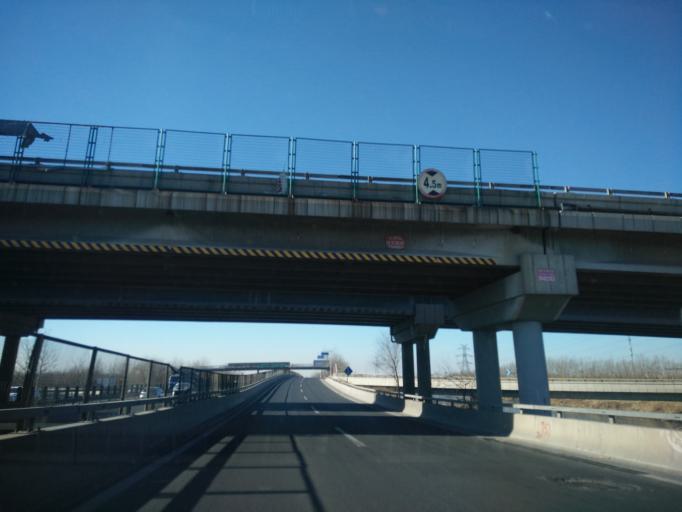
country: CN
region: Beijing
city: Qingyundian
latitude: 39.7390
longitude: 116.5147
